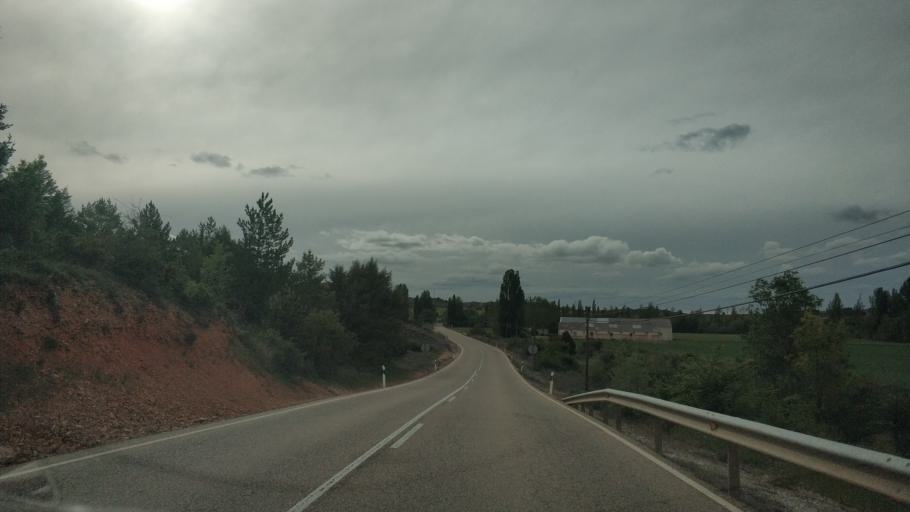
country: ES
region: Castille and Leon
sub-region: Provincia de Soria
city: El Burgo de Osma
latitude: 41.5784
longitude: -3.0331
